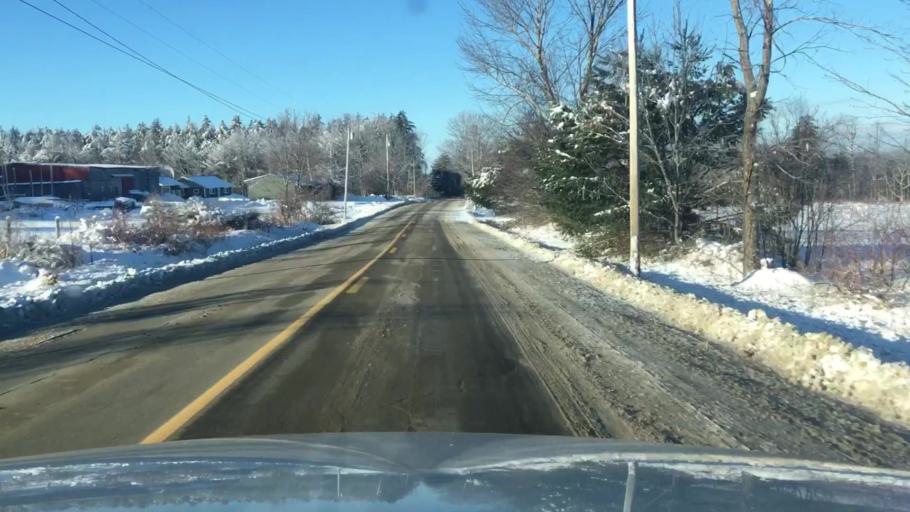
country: US
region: Maine
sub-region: Kennebec County
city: Readfield
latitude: 44.4314
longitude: -69.9531
